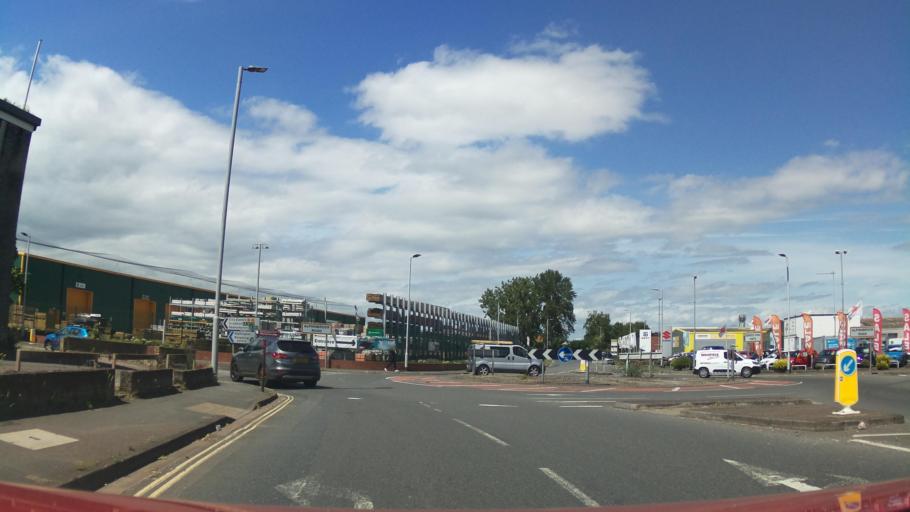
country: GB
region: England
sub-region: Devon
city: Exeter
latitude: 50.7035
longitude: -3.5257
